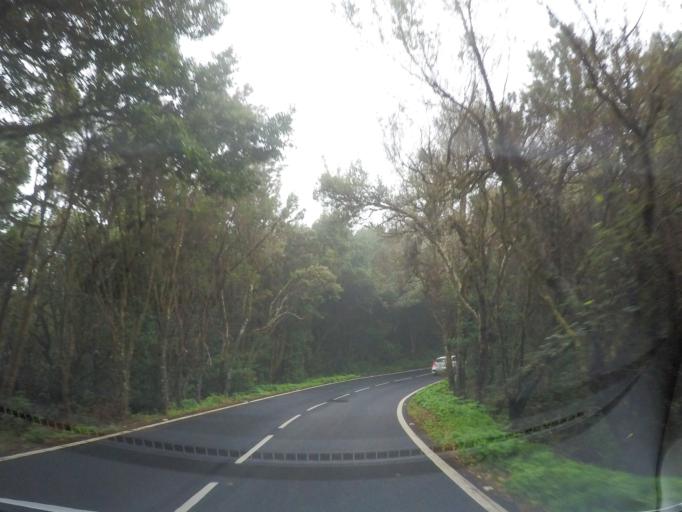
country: ES
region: Canary Islands
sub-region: Provincia de Santa Cruz de Tenerife
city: Vallehermosa
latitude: 28.1431
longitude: -17.2852
